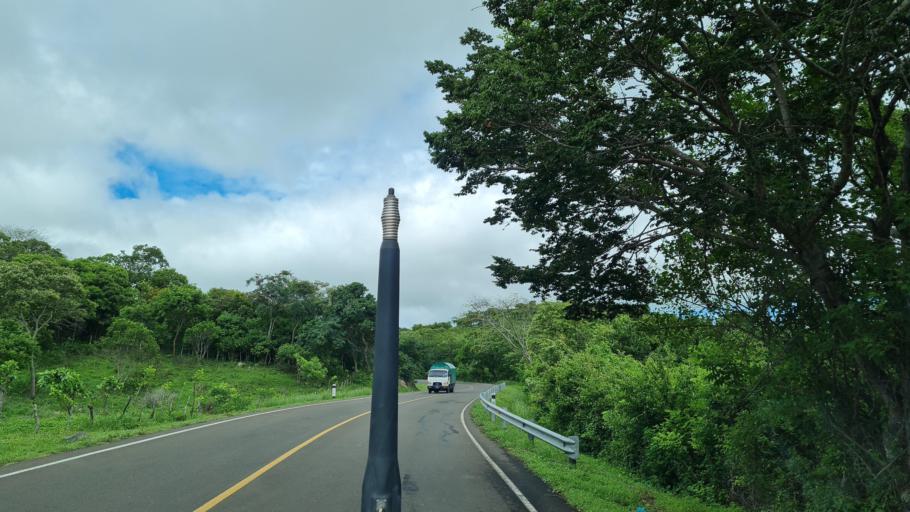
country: NI
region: Matagalpa
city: Terrabona
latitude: 12.5932
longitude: -85.9537
